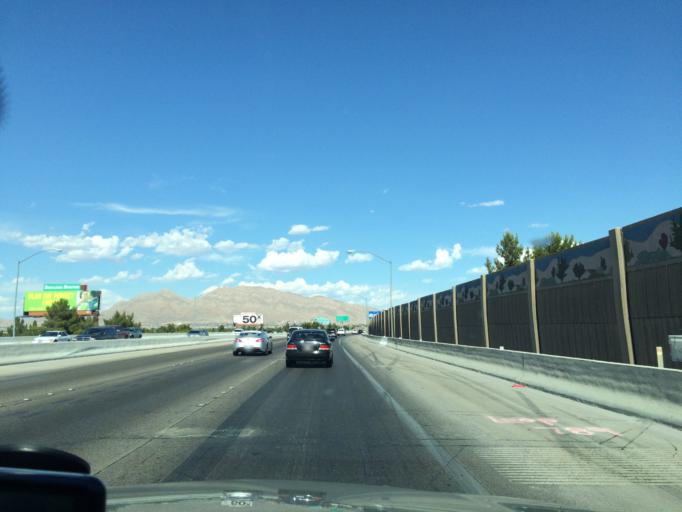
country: US
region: Nevada
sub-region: Clark County
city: Las Vegas
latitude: 36.1675
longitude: -115.1046
